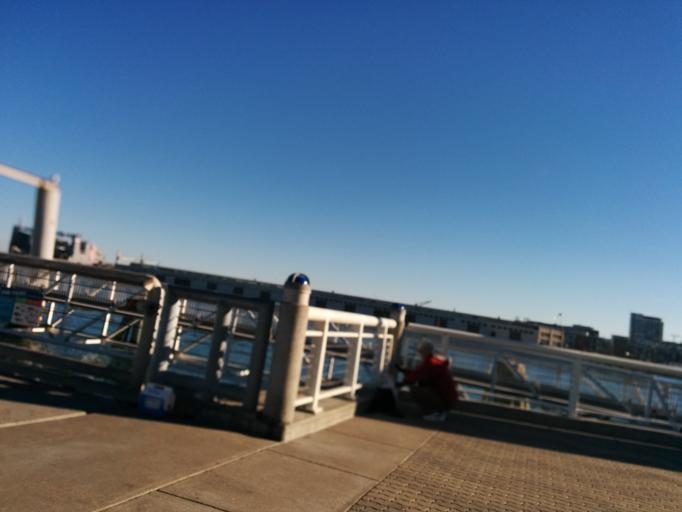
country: US
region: California
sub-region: San Francisco County
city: San Francisco
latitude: 37.7783
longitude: -122.3875
